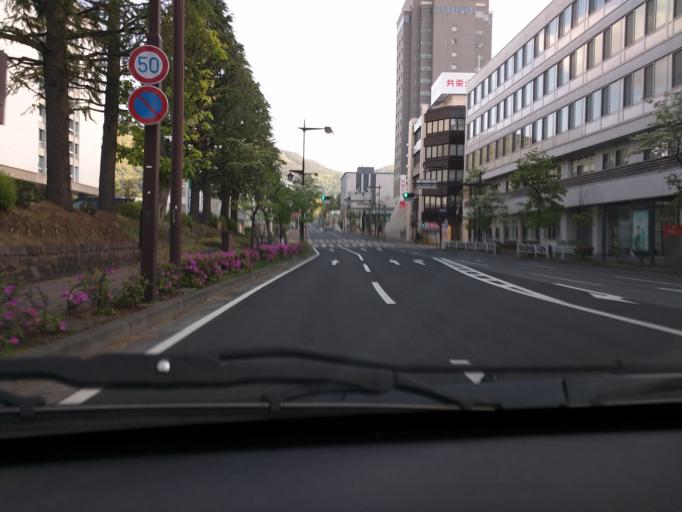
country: JP
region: Nagano
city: Nagano-shi
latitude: 36.6505
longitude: 138.1820
